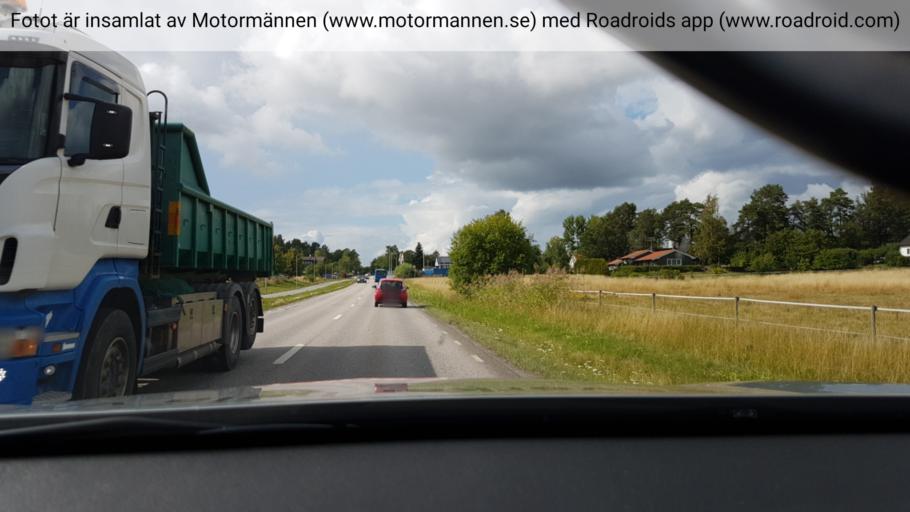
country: SE
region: Stockholm
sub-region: Ekero Kommun
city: Ekeroe
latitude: 59.3194
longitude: 17.7674
